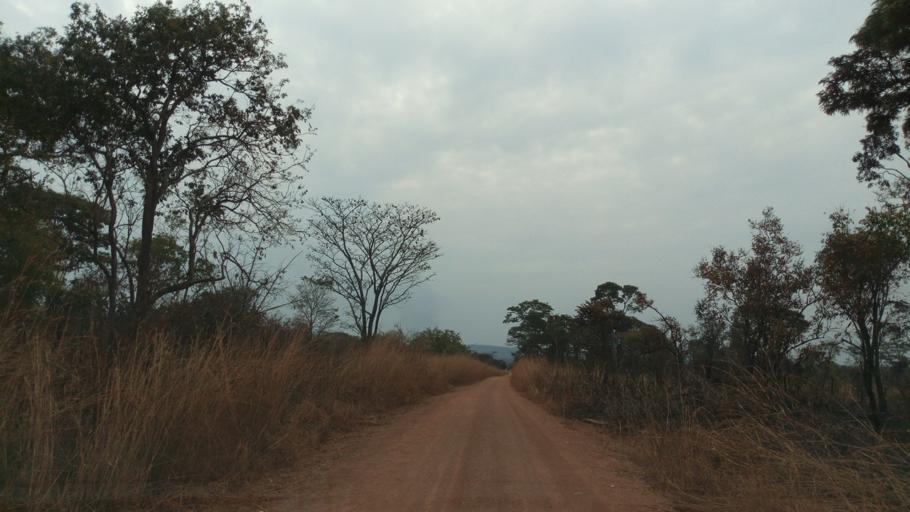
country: ZM
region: Northern
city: Kaputa
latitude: -8.1732
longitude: 29.0908
